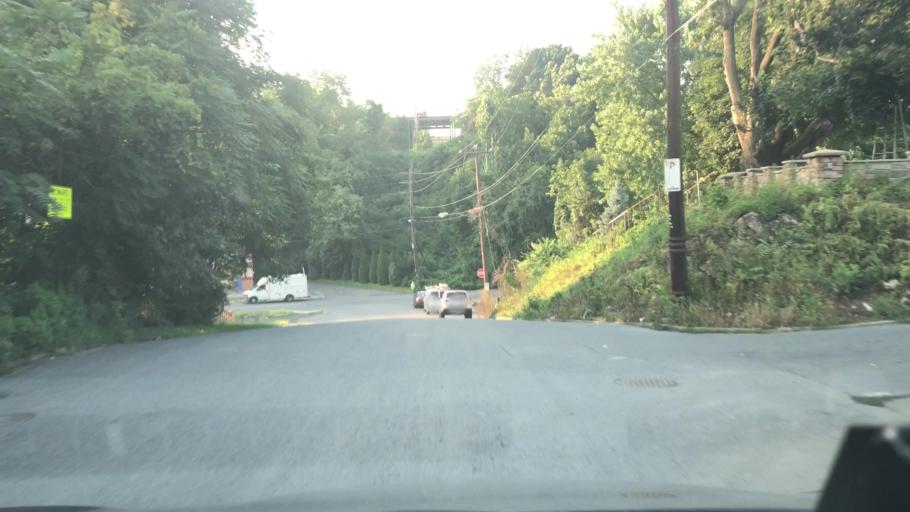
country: US
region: Pennsylvania
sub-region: Lehigh County
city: Allentown
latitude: 40.6151
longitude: -75.4800
